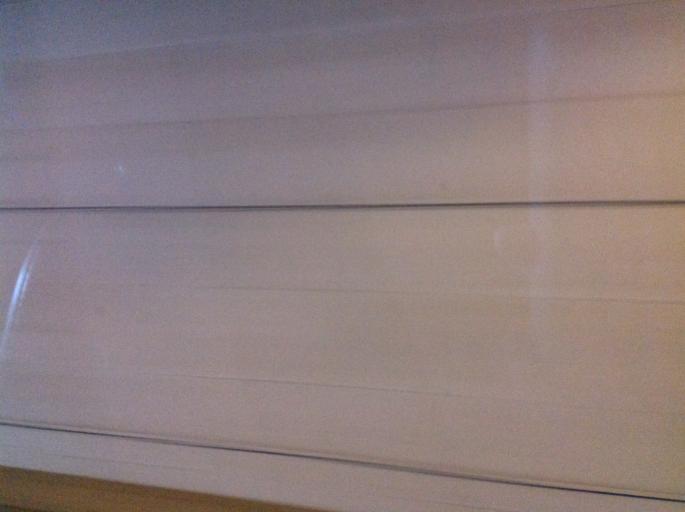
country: GR
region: Attica
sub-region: Nomarchia Anatolikis Attikis
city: Leondarion
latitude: 38.0008
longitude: 23.8455
